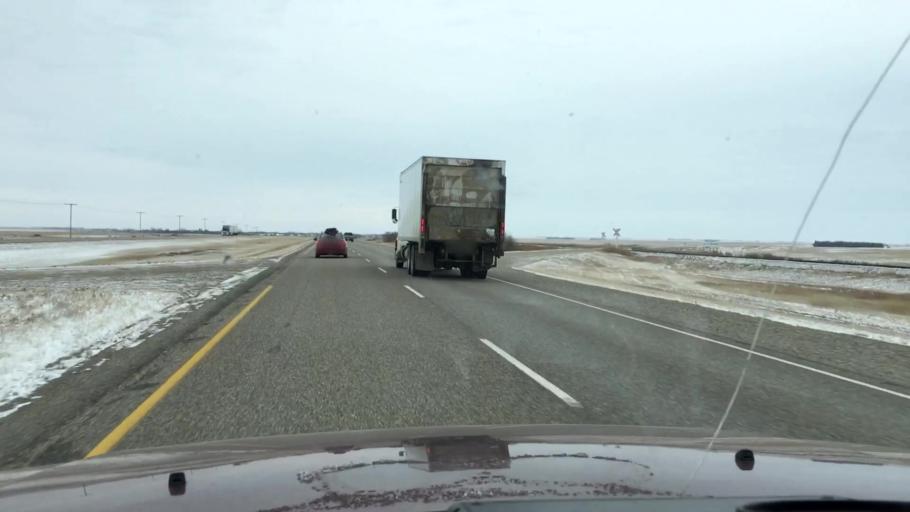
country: CA
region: Saskatchewan
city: Watrous
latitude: 51.1797
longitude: -105.9387
